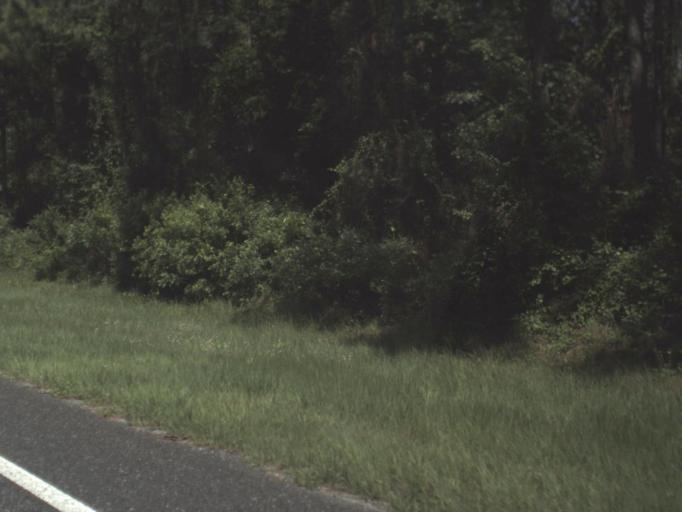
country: US
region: Florida
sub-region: Union County
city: Lake Butler
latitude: 30.2097
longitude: -82.3963
